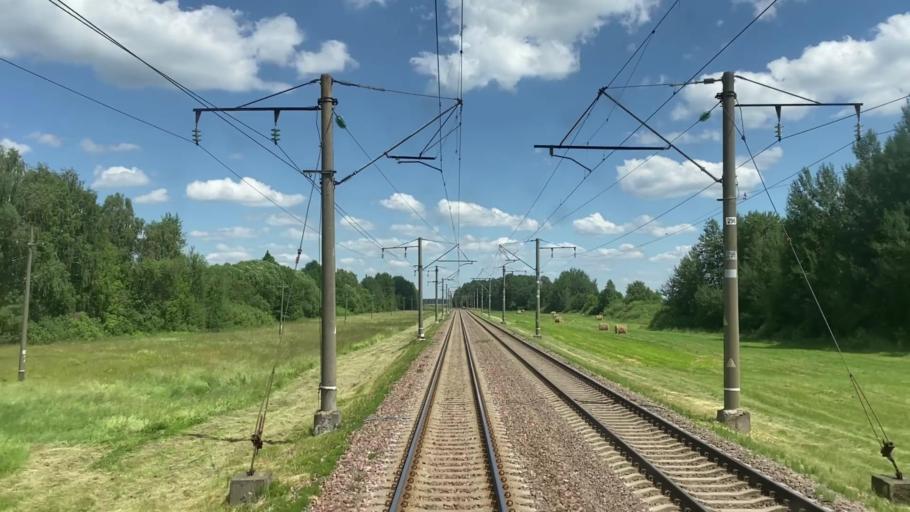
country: BY
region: Brest
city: Ivatsevichy
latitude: 52.7564
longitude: 25.3916
